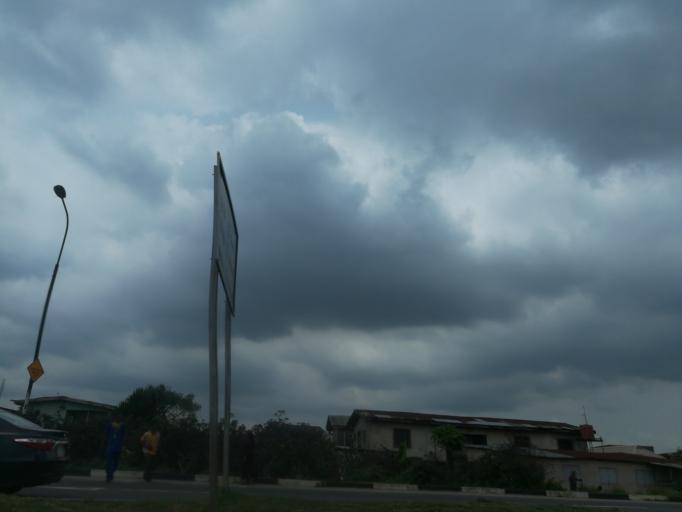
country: NG
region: Lagos
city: Somolu
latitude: 6.5484
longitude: 3.3971
